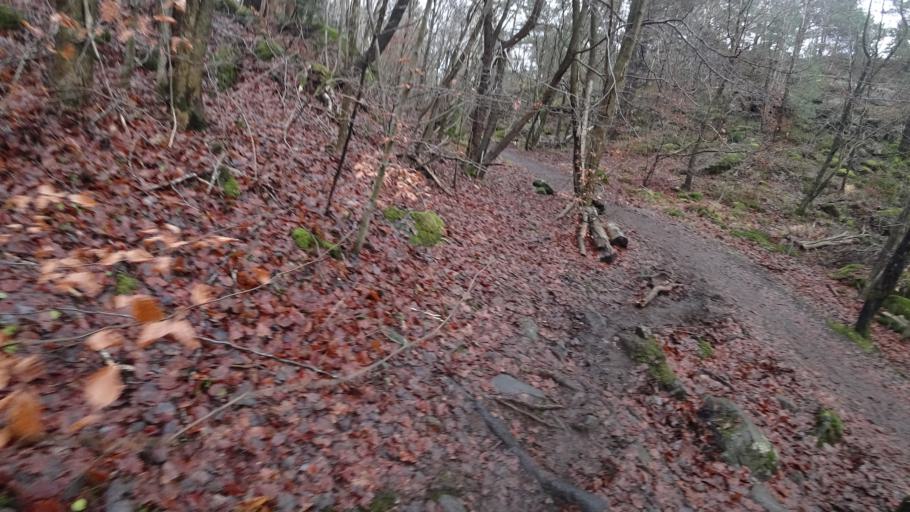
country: SE
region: Vaestra Goetaland
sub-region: Goteborg
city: Goeteborg
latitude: 57.6672
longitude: 11.9535
